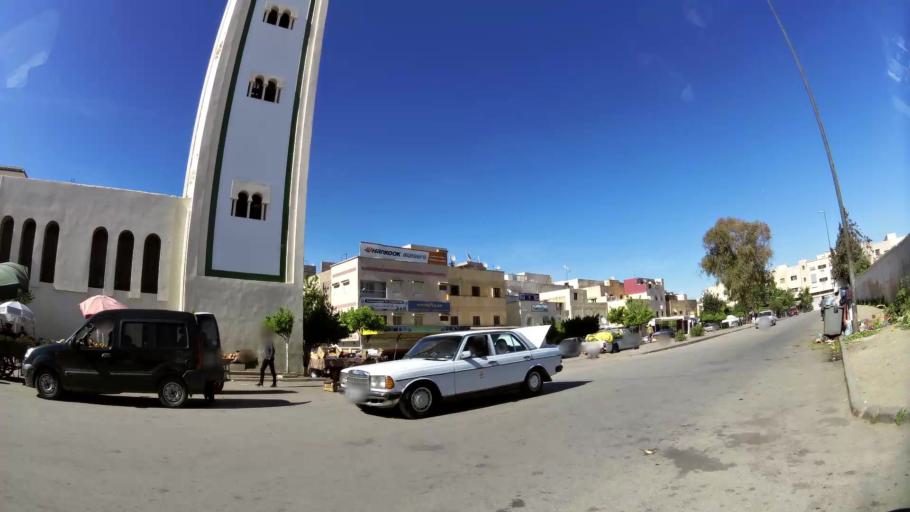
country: MA
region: Fes-Boulemane
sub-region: Fes
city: Fes
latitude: 34.0203
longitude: -4.9762
